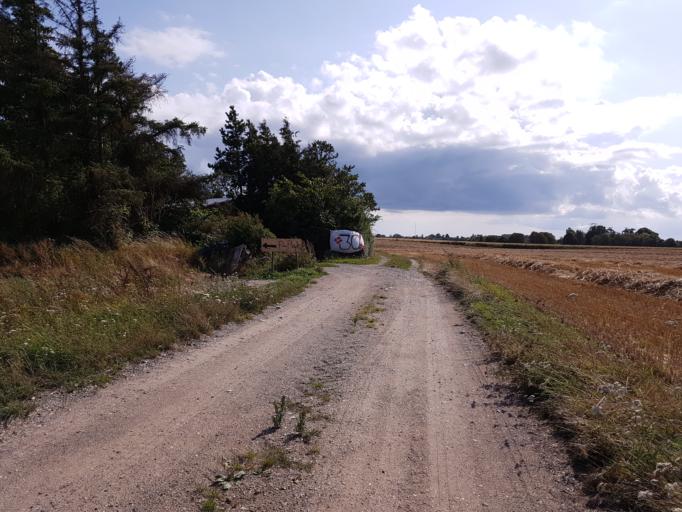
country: DK
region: Zealand
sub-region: Guldborgsund Kommune
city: Nykobing Falster
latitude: 54.5901
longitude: 11.9360
